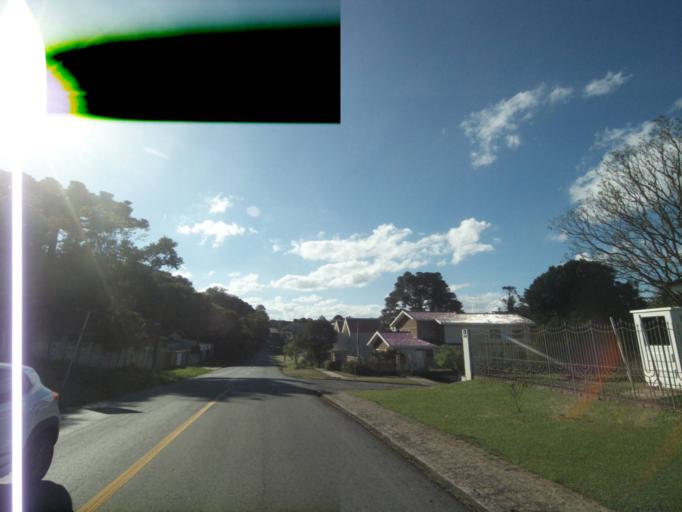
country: BR
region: Parana
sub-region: Curitiba
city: Curitiba
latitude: -25.3951
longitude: -49.2539
